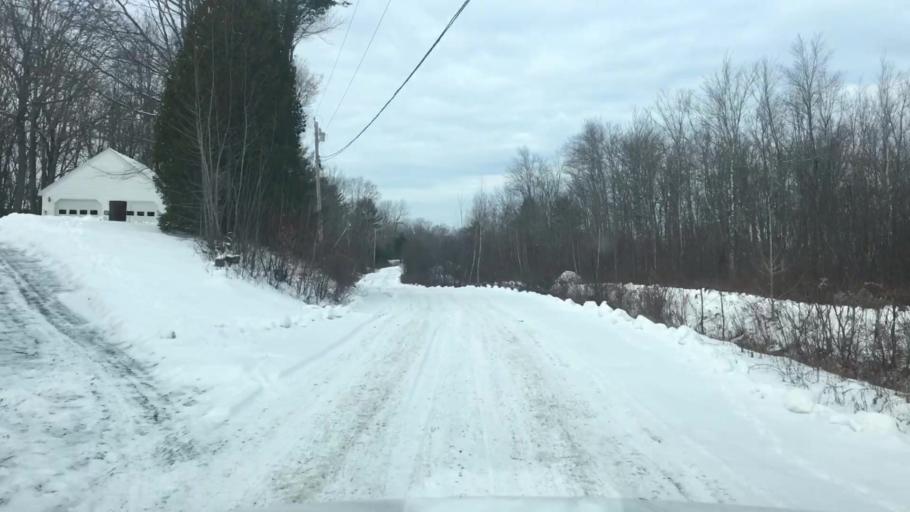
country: US
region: Maine
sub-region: Kennebec County
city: Chelsea
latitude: 44.2942
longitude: -69.6585
